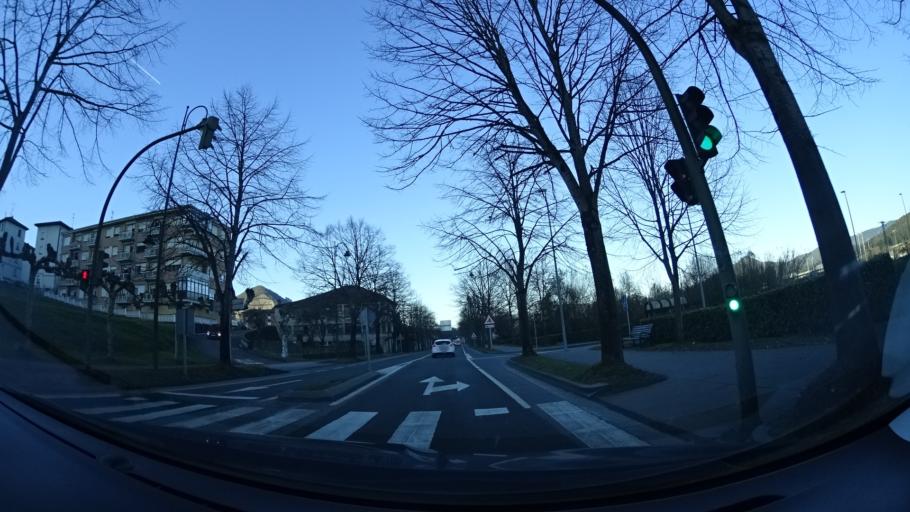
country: ES
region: Basque Country
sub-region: Bizkaia
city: Gernika-Lumo
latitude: 43.3215
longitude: -2.6784
